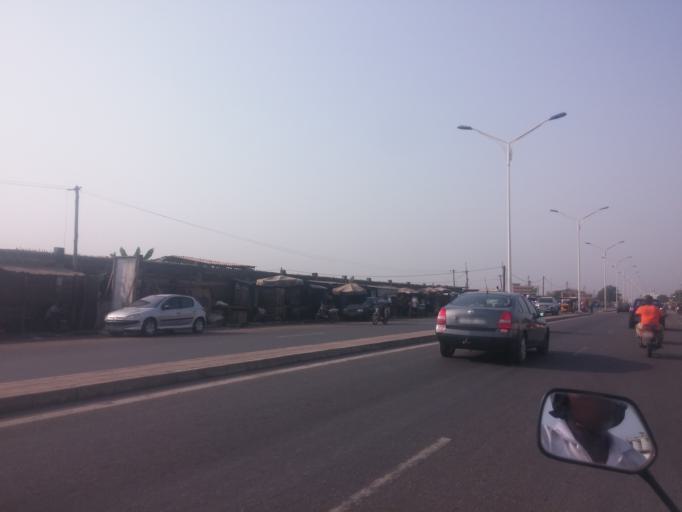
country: TG
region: Maritime
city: Lome
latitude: 6.1532
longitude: 1.2861
